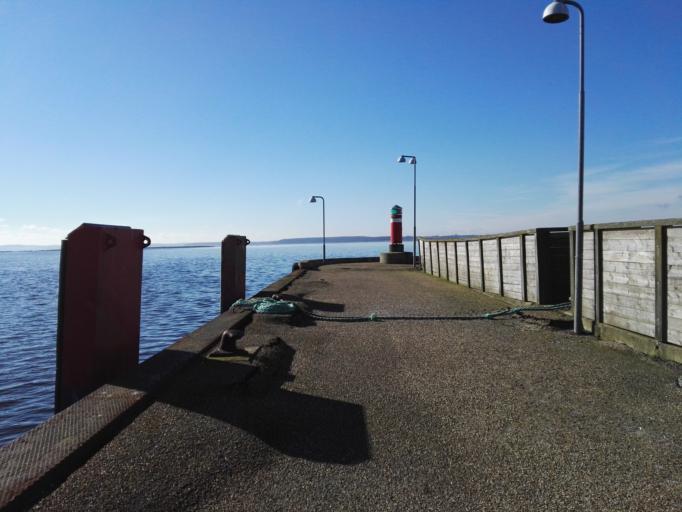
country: DK
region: Zealand
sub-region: Lejre Kommune
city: Ejby
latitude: 55.7550
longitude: 11.7994
